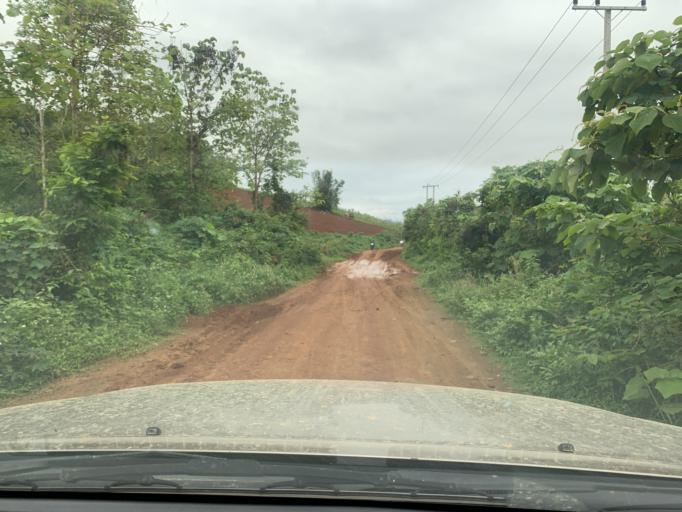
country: TH
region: Nan
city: Mae Charim
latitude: 18.4160
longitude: 101.4445
